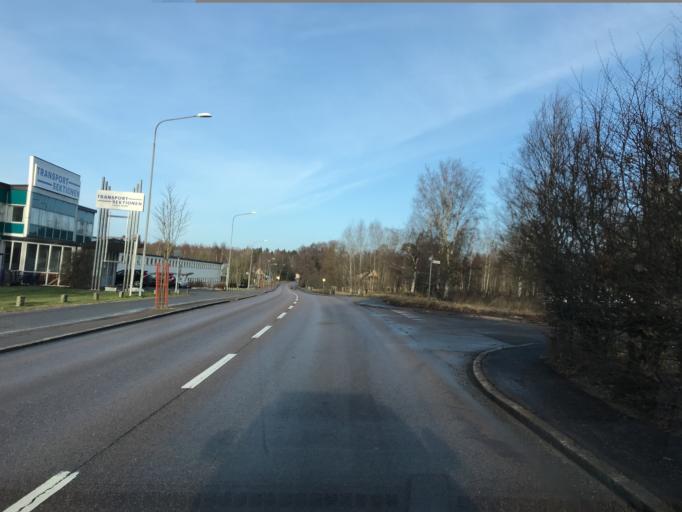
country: SE
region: Skane
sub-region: Hassleholms Kommun
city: Bjarnum
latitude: 56.2999
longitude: 13.7039
